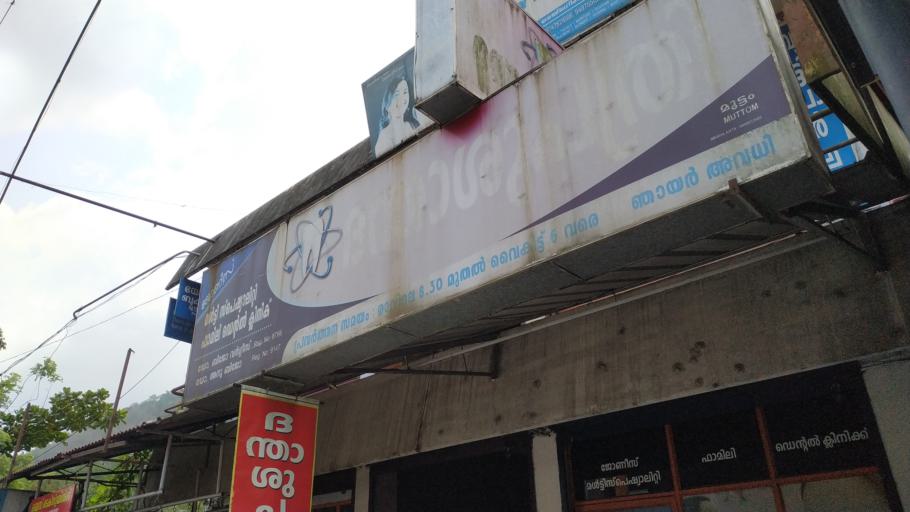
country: IN
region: Kerala
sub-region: Kottayam
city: Lalam
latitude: 9.8379
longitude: 76.7462
